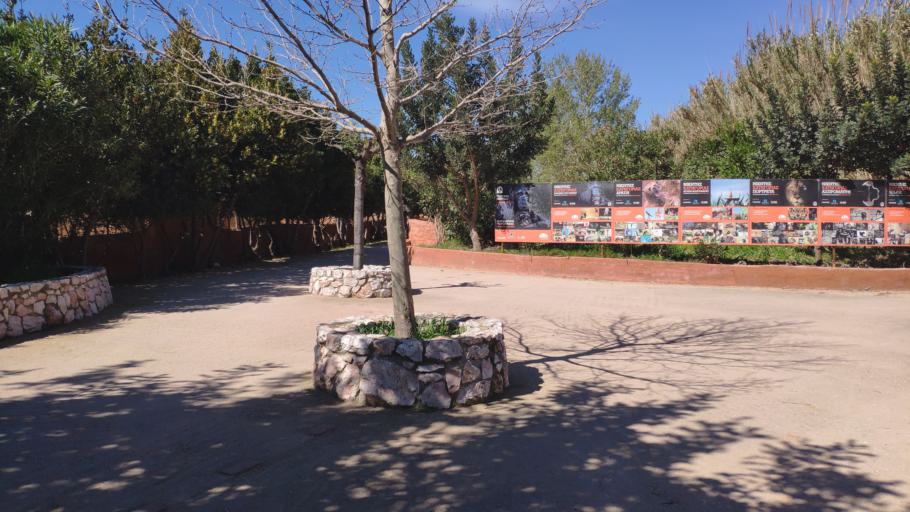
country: GR
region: Attica
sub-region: Nomarchia Anatolikis Attikis
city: Spata
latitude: 37.9810
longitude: 23.9109
